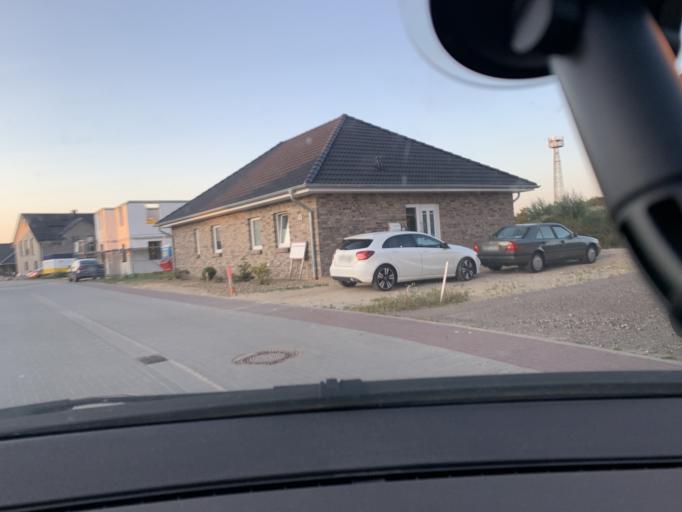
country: DE
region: Schleswig-Holstein
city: Mildstedt
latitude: 54.4627
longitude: 9.1044
